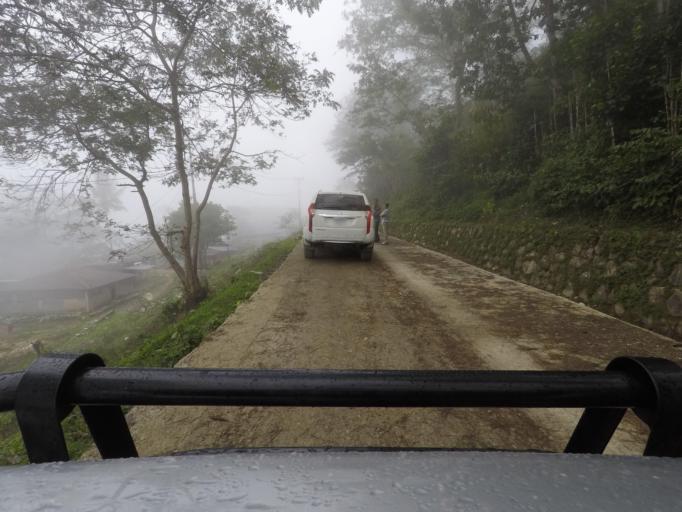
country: TL
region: Bobonaro
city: Maliana
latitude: -9.0336
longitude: 125.3179
